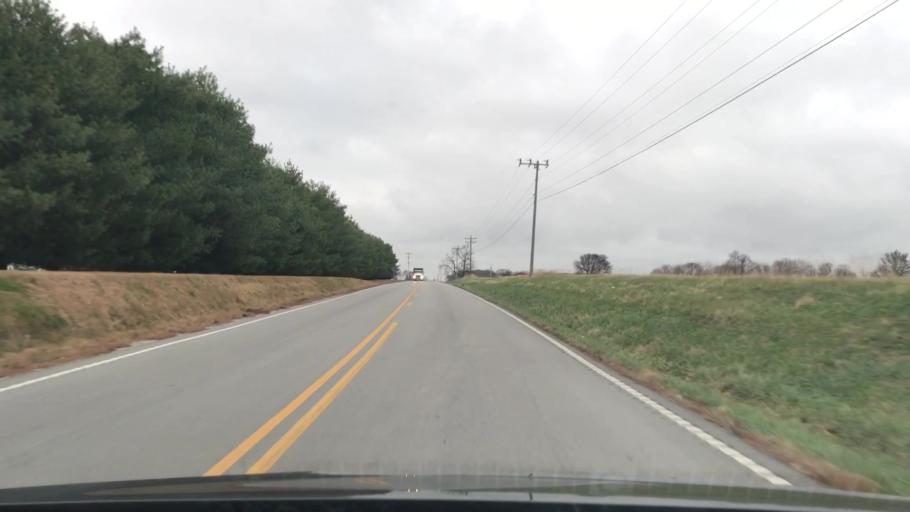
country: US
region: Kentucky
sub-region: Todd County
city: Guthrie
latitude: 36.6721
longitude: -87.1980
